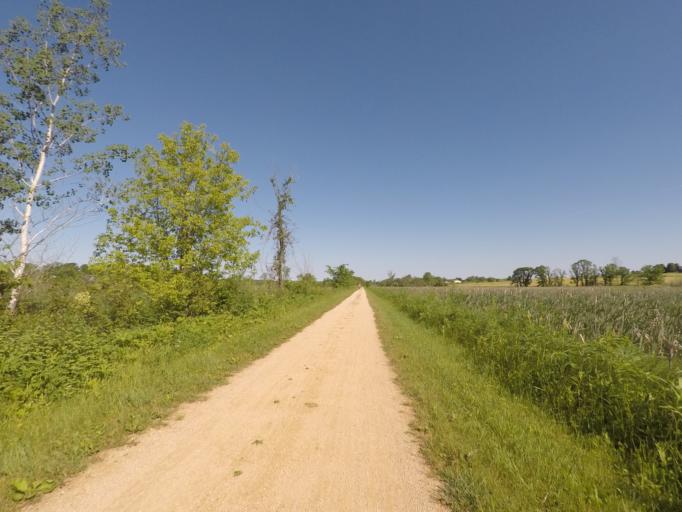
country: US
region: Wisconsin
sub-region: Dane County
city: Verona
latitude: 43.0002
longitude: -89.5856
